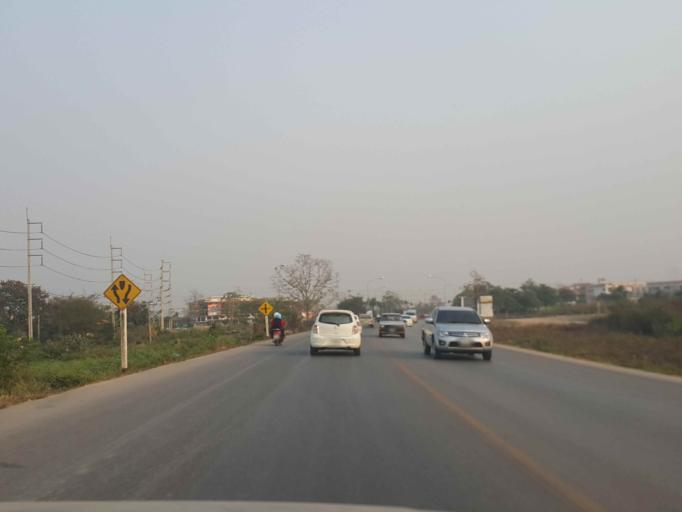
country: TH
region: Chiang Mai
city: San Sai
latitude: 18.8281
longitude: 99.0465
